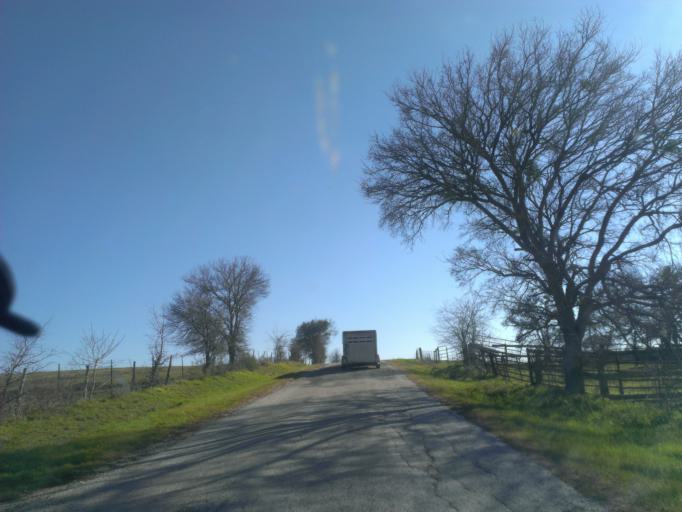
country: US
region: Texas
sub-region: Milam County
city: Thorndale
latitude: 30.5120
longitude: -97.2453
